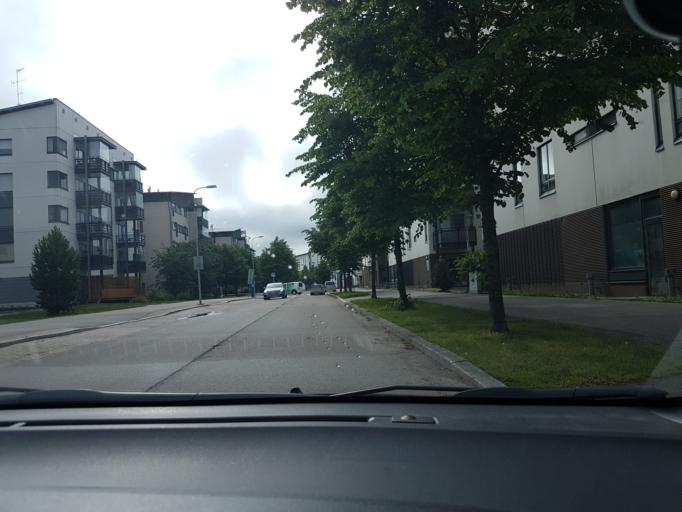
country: FI
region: Uusimaa
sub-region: Helsinki
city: Vantaa
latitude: 60.2640
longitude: 25.0365
